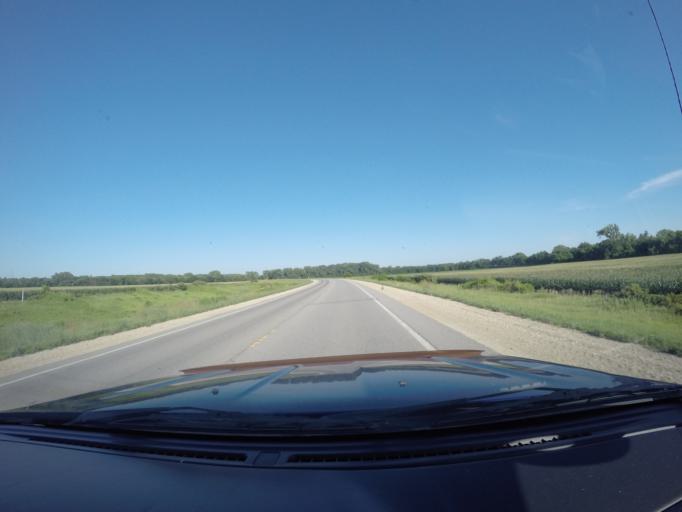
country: US
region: Kansas
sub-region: Jefferson County
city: Oskaloosa
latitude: 39.0819
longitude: -95.4051
